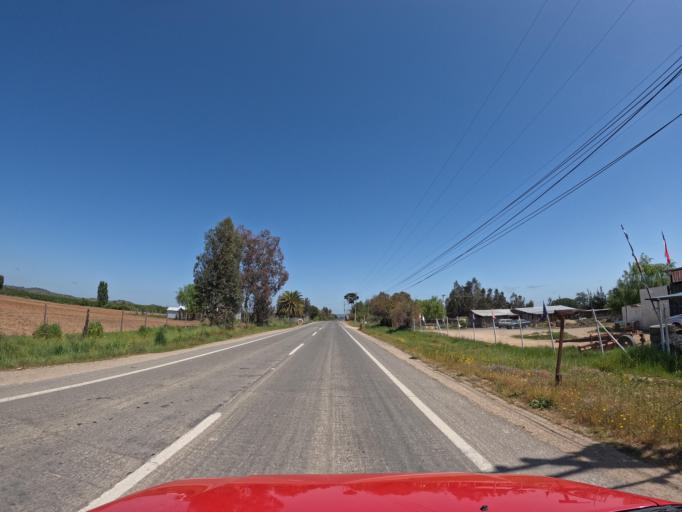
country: CL
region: O'Higgins
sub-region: Provincia de Colchagua
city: Santa Cruz
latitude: -34.7337
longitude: -71.6886
